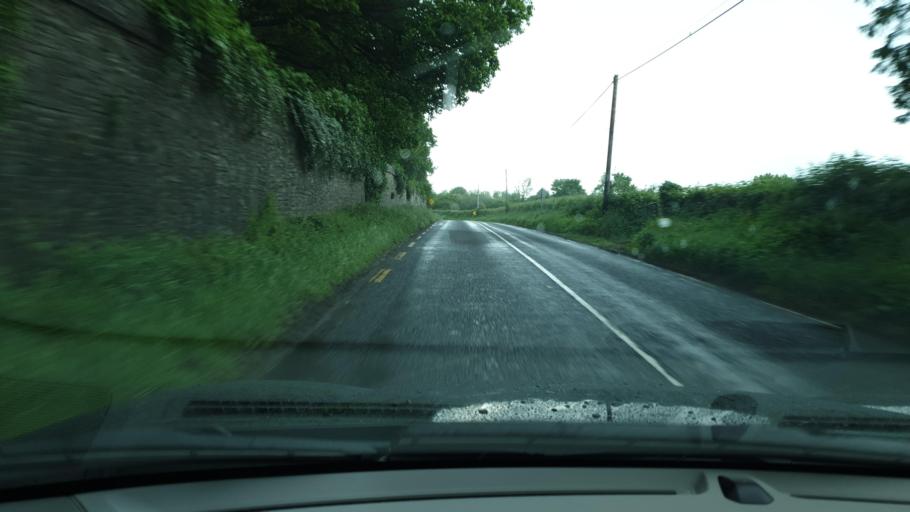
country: IE
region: Leinster
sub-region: Laois
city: Mountrath
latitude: 53.0607
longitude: -7.4157
